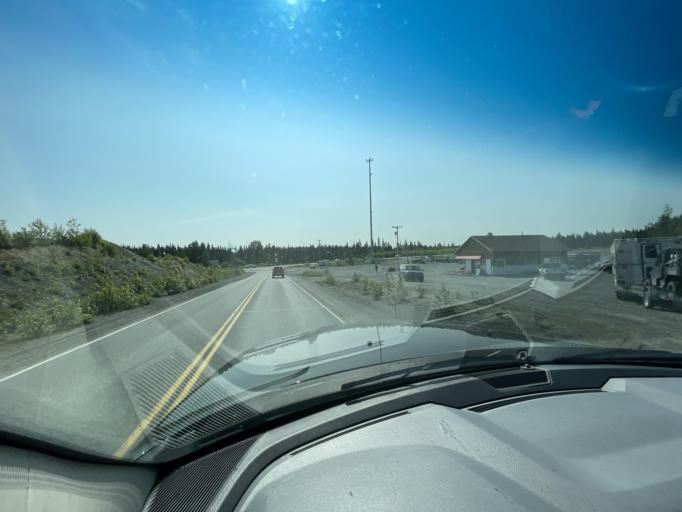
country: US
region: Alaska
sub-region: Kenai Peninsula Borough
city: Cohoe
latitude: 60.2976
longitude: -151.2776
